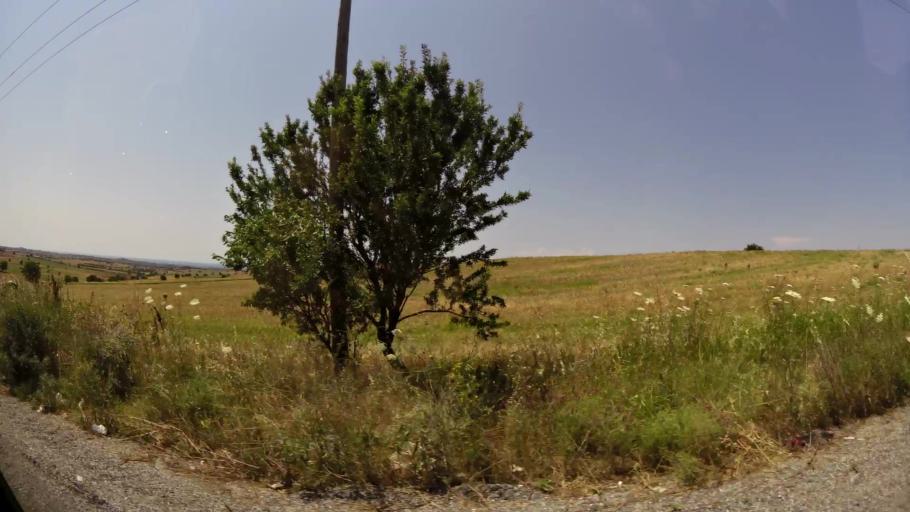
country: GR
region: Central Macedonia
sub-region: Nomos Thessalonikis
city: Neoi Epivates
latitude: 40.4657
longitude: 22.9024
